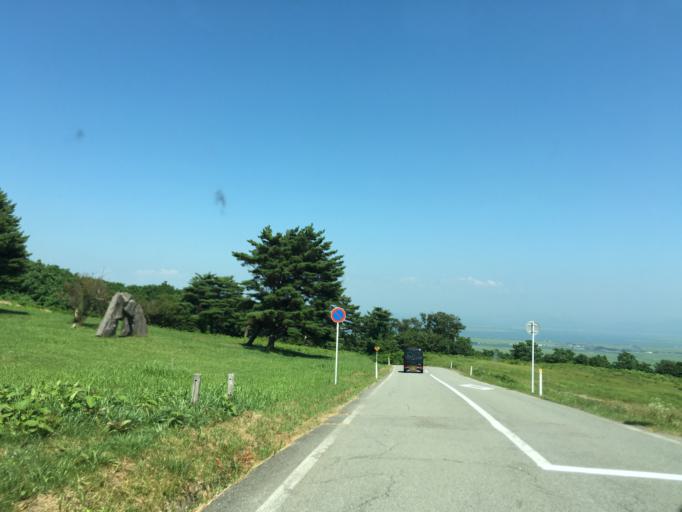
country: JP
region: Akita
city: Tenno
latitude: 39.9273
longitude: 139.8770
